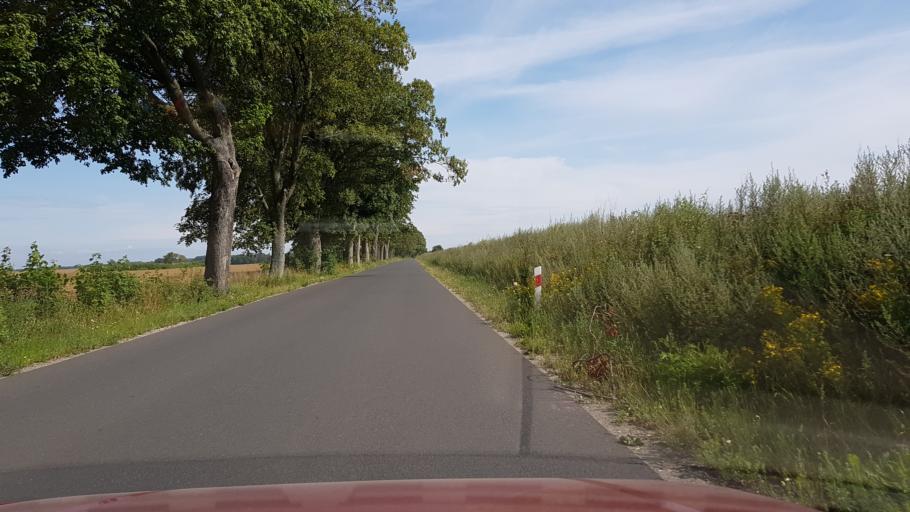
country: PL
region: West Pomeranian Voivodeship
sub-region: Powiat koszalinski
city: Polanow
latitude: 54.1397
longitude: 16.6211
